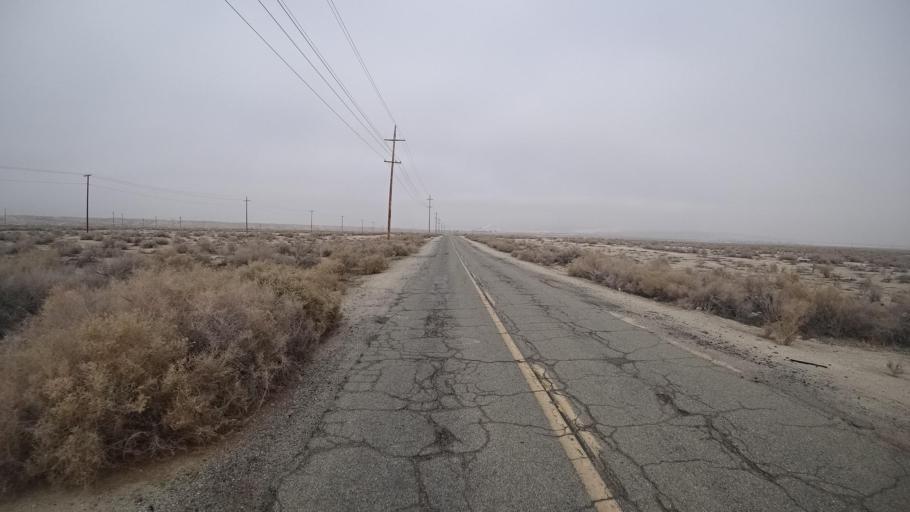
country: US
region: California
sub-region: Kern County
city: Maricopa
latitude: 35.0954
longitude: -119.4020
